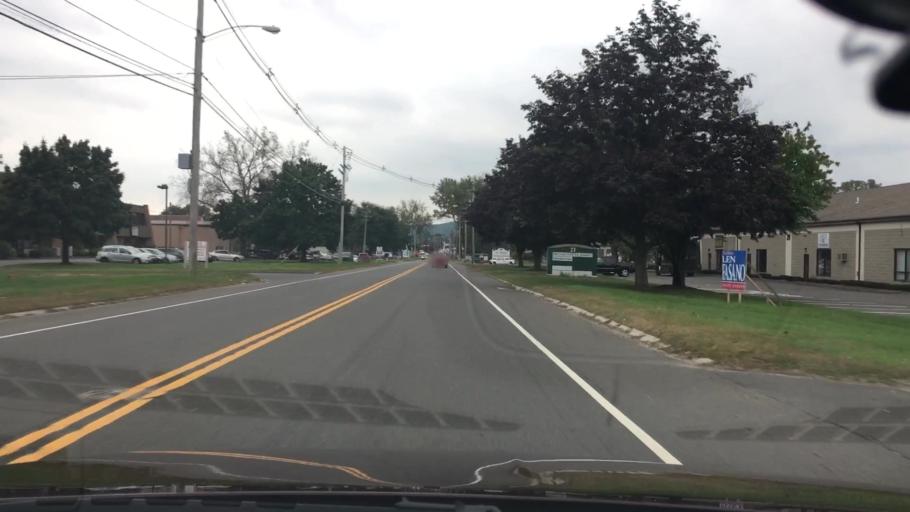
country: US
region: Connecticut
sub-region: New Haven County
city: Wallingford
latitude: 41.4861
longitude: -72.8133
